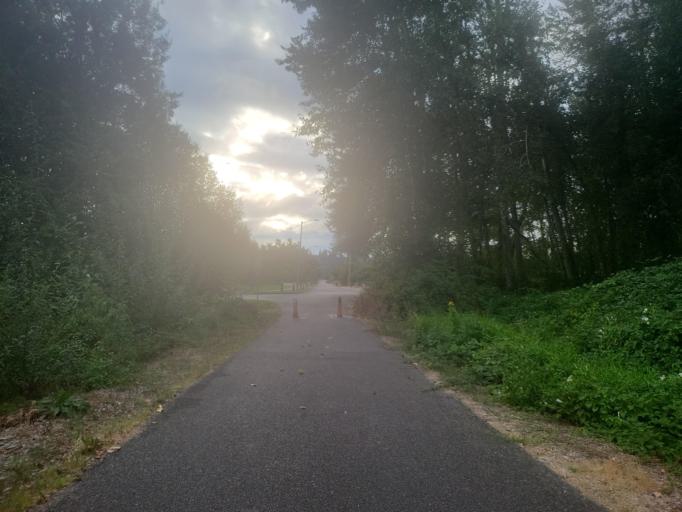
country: US
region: Washington
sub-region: King County
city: Pacific
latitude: 47.2428
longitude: -122.2357
